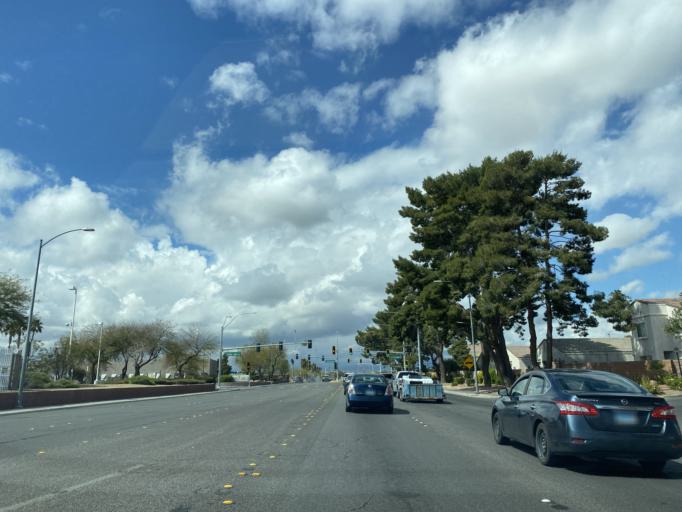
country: US
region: Nevada
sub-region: Clark County
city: Las Vegas
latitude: 36.1958
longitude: -115.1634
